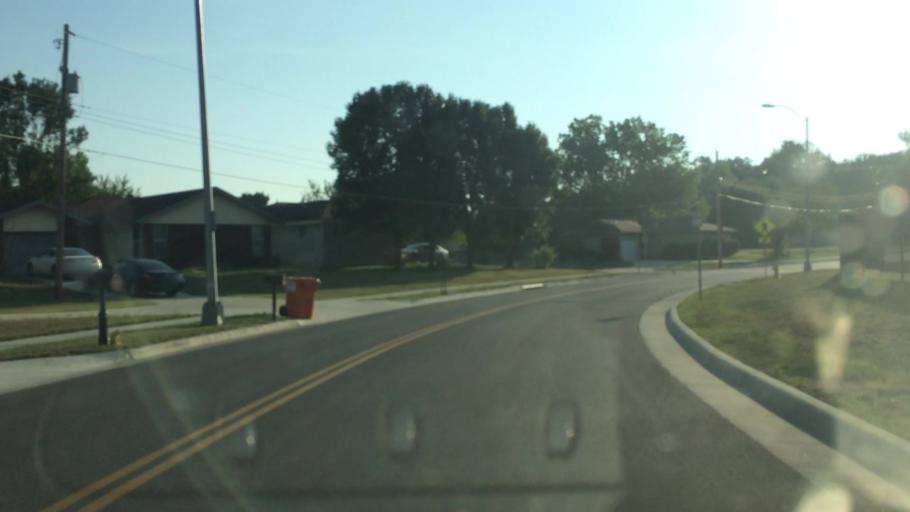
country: US
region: Missouri
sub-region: Greene County
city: Springfield
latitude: 37.2185
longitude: -93.2800
